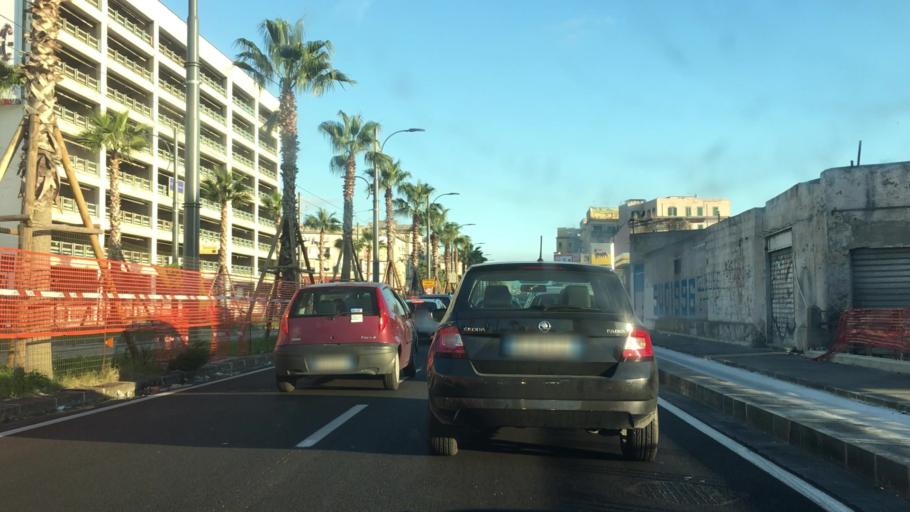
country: IT
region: Campania
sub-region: Provincia di Napoli
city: Napoli
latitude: 40.8462
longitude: 14.2787
